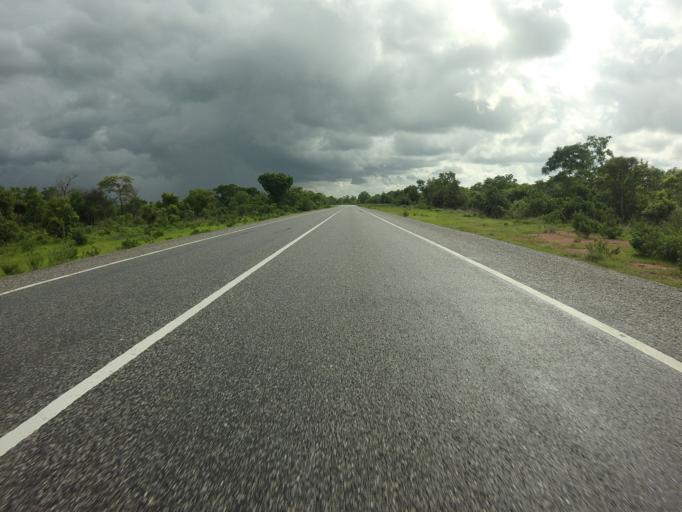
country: GH
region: Northern
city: Tamale
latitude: 9.1671
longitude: -1.4804
